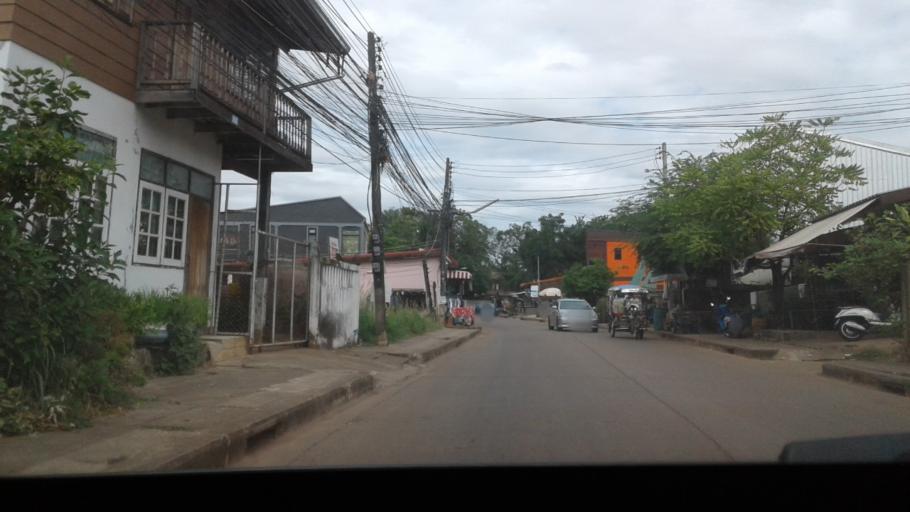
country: TH
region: Changwat Udon Thani
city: Udon Thani
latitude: 17.4239
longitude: 102.7832
